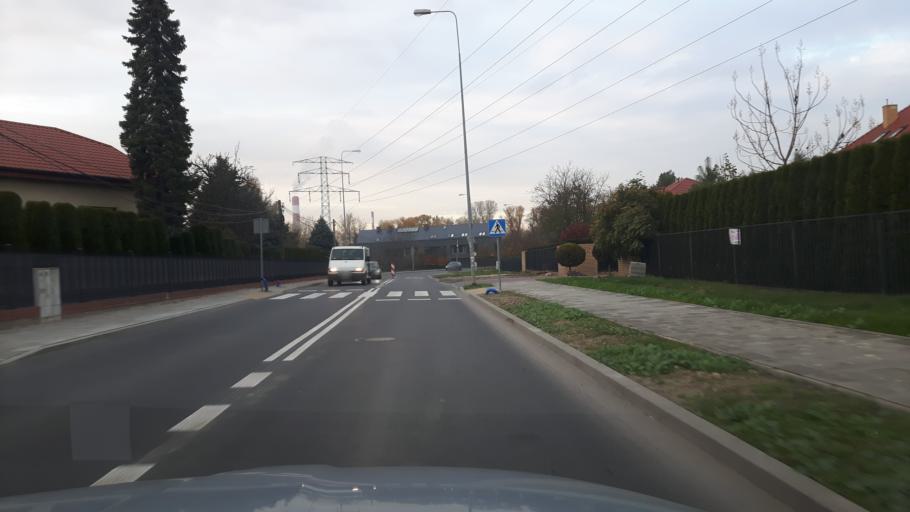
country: PL
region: Masovian Voivodeship
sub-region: Warszawa
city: Wilanow
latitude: 52.1743
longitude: 21.1080
